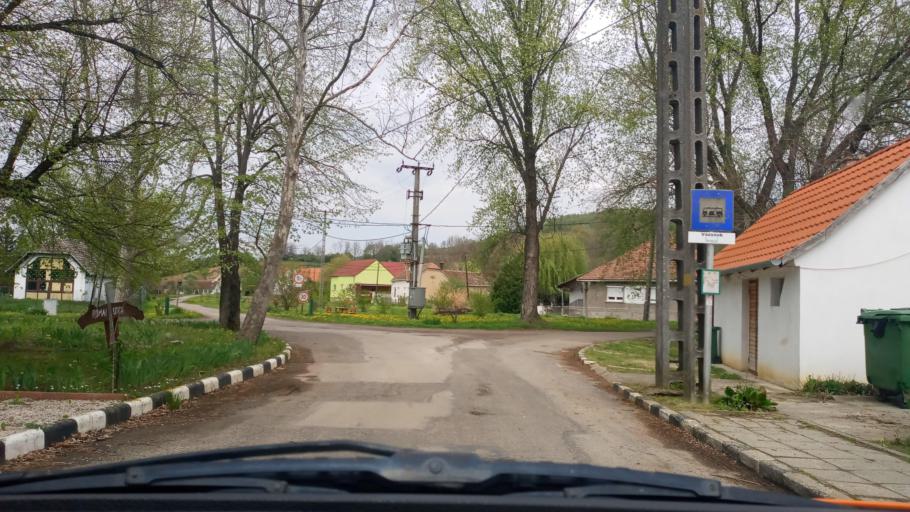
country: HU
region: Baranya
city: Sasd
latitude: 46.2645
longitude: 18.1245
